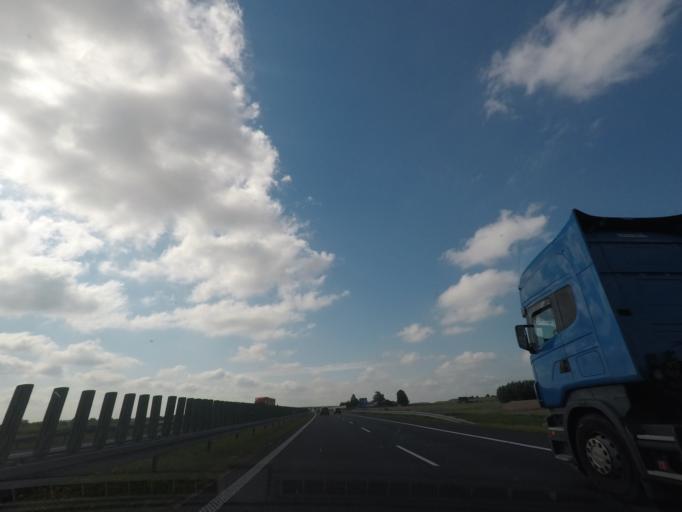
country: PL
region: Pomeranian Voivodeship
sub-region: Powiat starogardzki
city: Smetowo Graniczne
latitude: 53.6971
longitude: 18.6276
